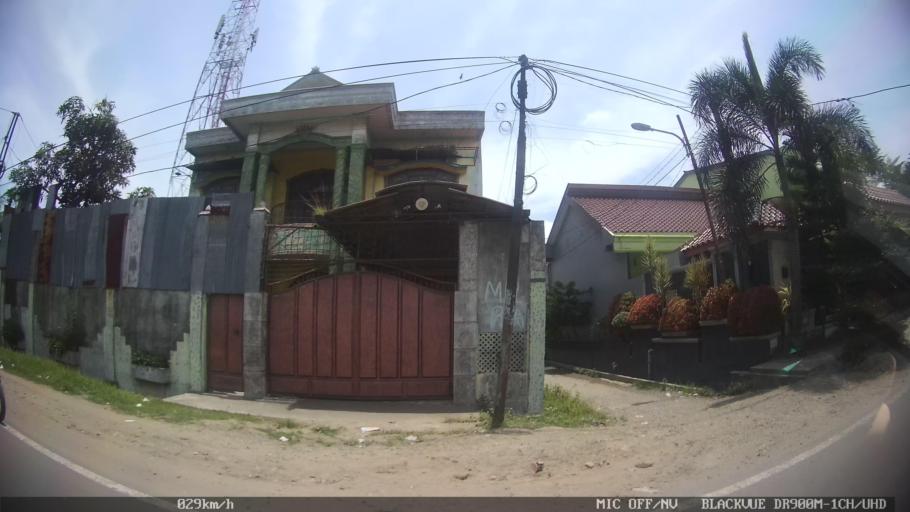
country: ID
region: North Sumatra
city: Labuhan Deli
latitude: 3.7378
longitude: 98.6762
